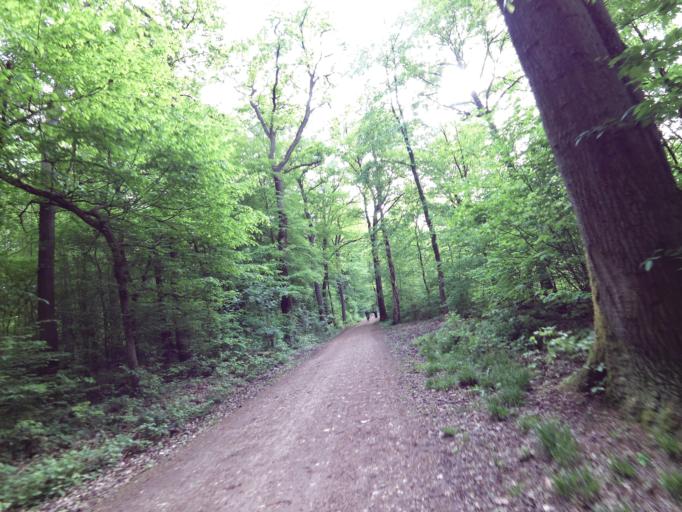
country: DE
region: North Rhine-Westphalia
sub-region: Regierungsbezirk Koln
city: Bonn
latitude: 50.6893
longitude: 7.0936
